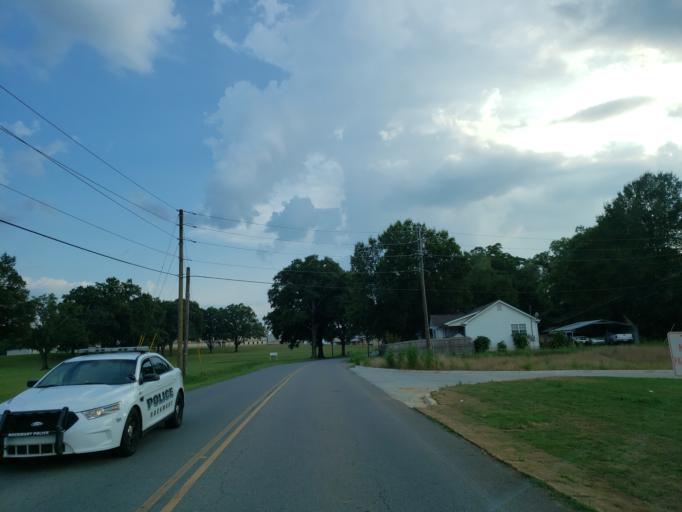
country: US
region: Georgia
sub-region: Polk County
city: Rockmart
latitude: 34.0052
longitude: -85.0304
